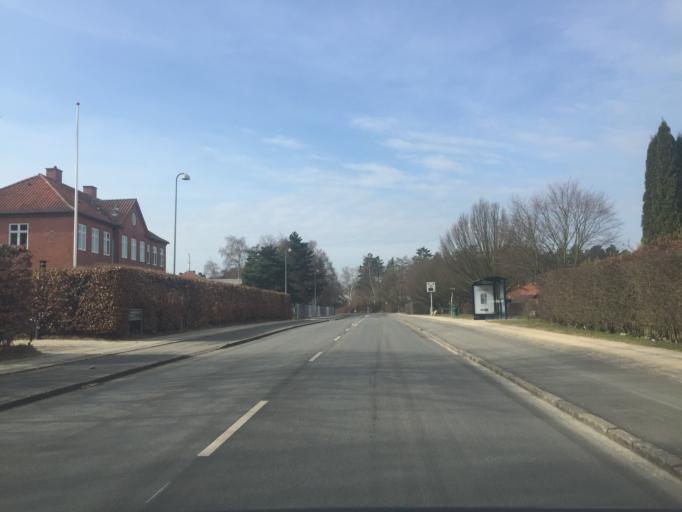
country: DK
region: Capital Region
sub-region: Lyngby-Tarbaek Kommune
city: Kongens Lyngby
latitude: 55.7892
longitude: 12.4816
